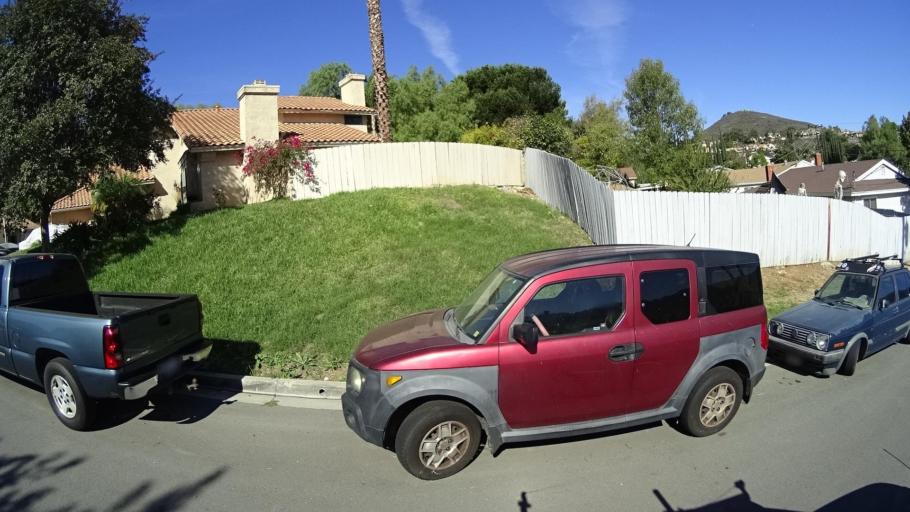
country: US
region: California
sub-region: San Diego County
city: La Presa
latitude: 32.7158
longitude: -116.9775
